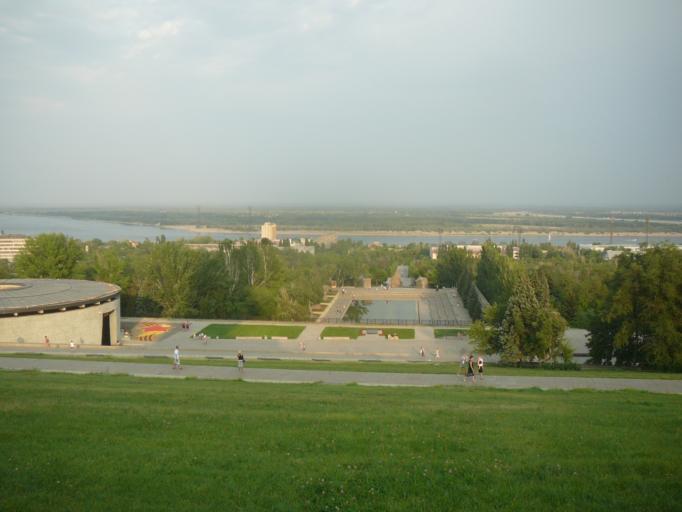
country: RU
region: Volgograd
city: Volgograd
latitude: 48.7423
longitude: 44.5372
